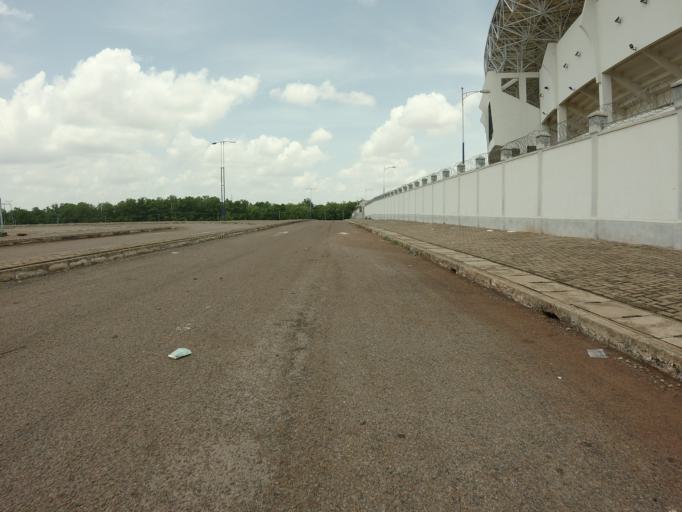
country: GH
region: Northern
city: Tamale
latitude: 9.4114
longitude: -0.8611
